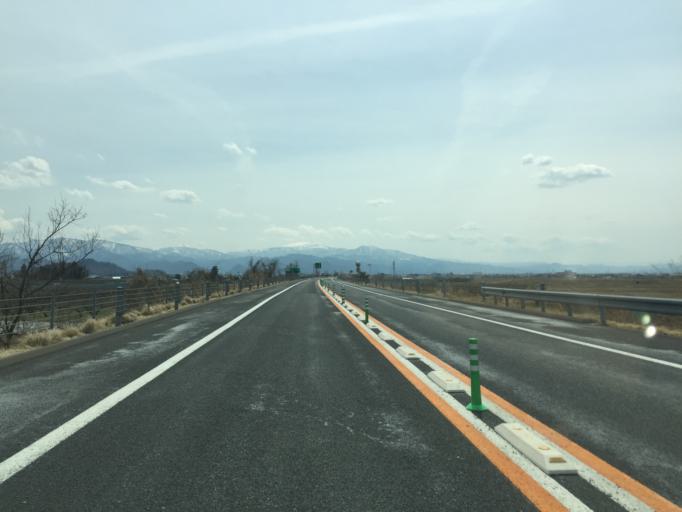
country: JP
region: Yamagata
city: Tendo
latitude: 38.3865
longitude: 140.3444
